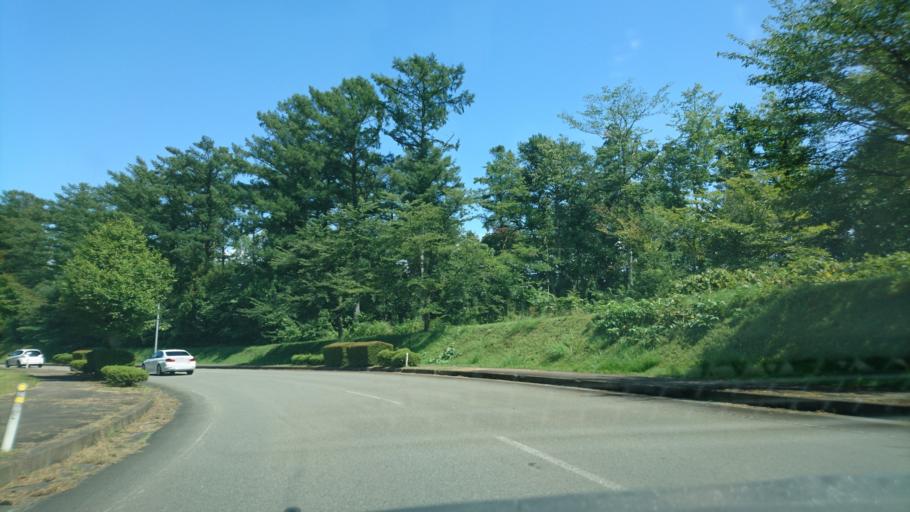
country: JP
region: Iwate
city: Morioka-shi
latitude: 39.8067
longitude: 141.1319
